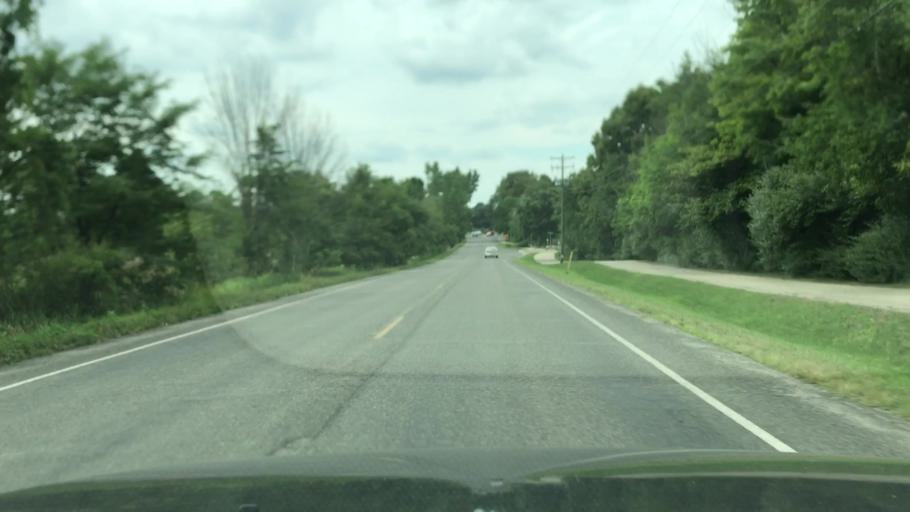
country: US
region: Michigan
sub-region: Kent County
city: East Grand Rapids
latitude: 42.9811
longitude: -85.5609
